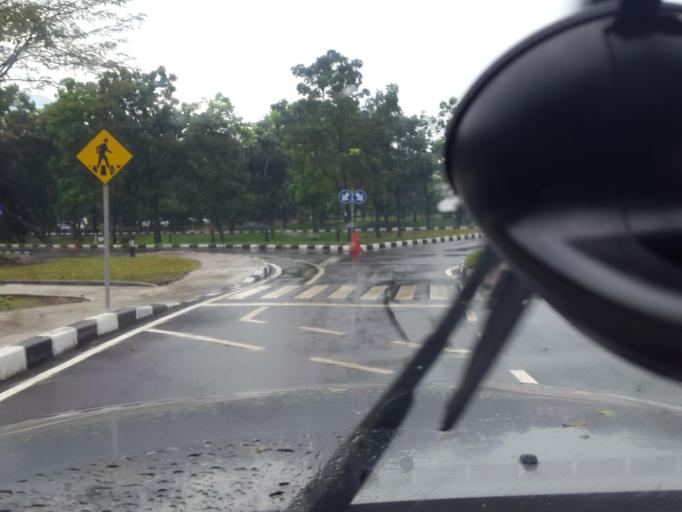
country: ID
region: West Java
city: Bandung
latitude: -6.9101
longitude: 107.6843
